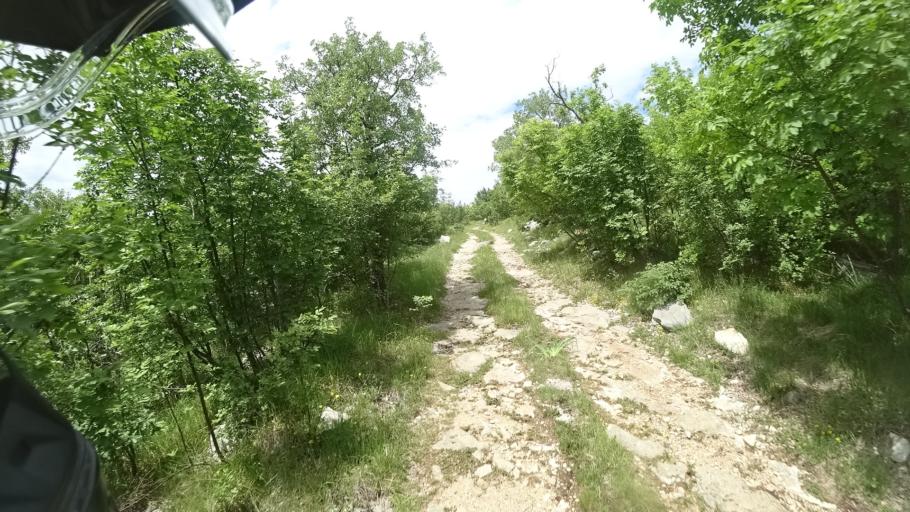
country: HR
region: Splitsko-Dalmatinska
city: Hrvace
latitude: 43.8831
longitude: 16.5829
